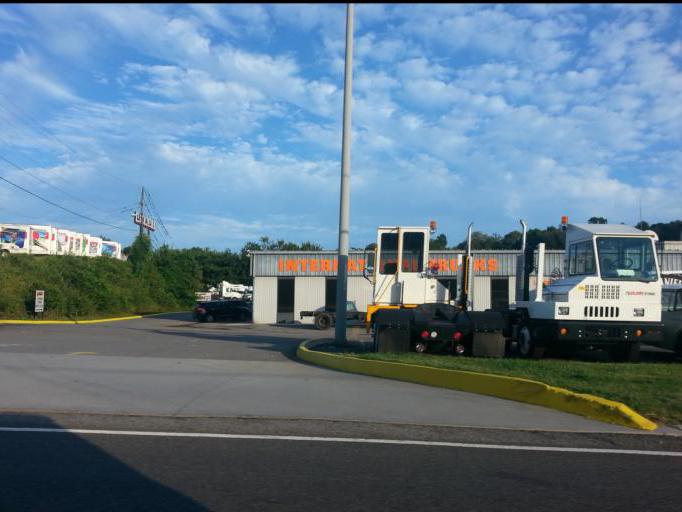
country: US
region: Tennessee
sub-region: Knox County
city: Knoxville
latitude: 36.0106
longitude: -83.8703
